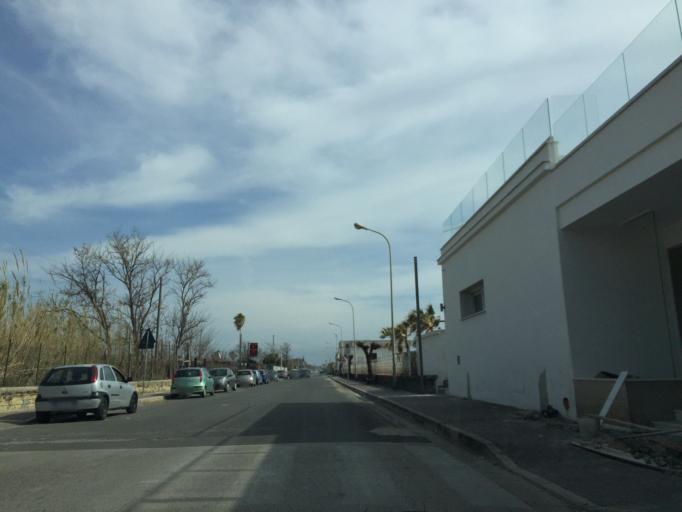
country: IT
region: Campania
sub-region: Provincia di Napoli
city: Bacoli
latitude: 40.7892
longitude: 14.0675
